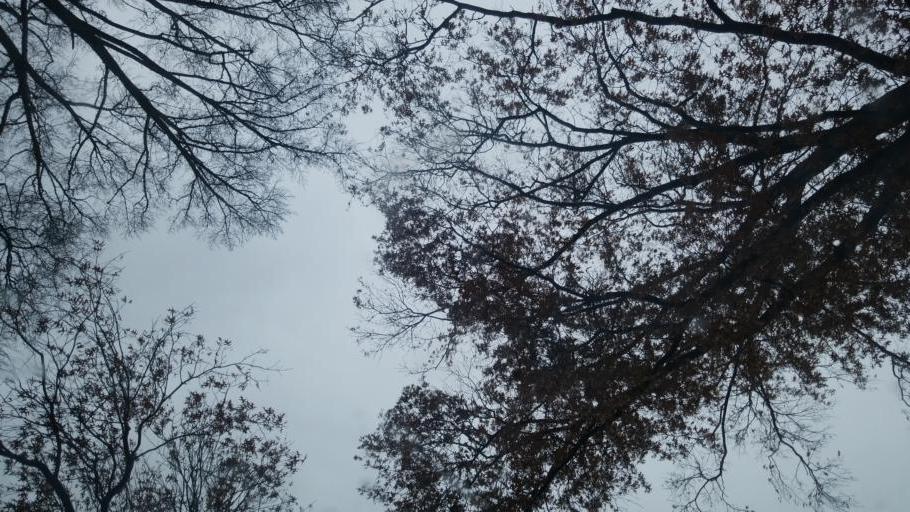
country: US
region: Maryland
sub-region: Prince George's County
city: Silver Hill
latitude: 38.8584
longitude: -76.9569
